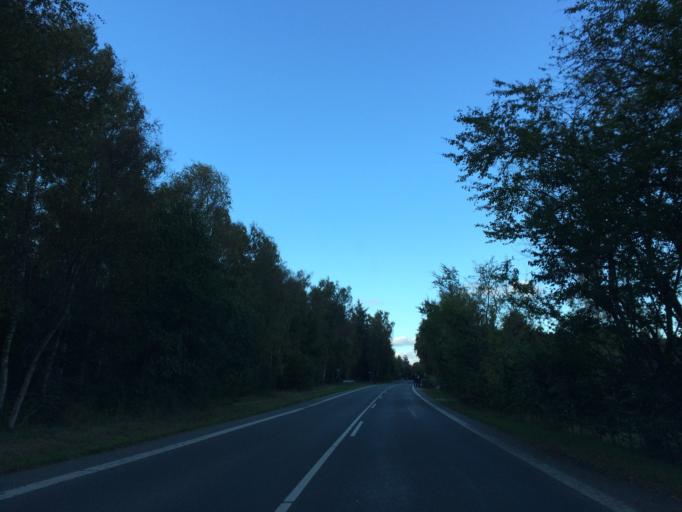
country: DK
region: Central Jutland
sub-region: Skanderborg Kommune
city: Ry
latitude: 56.0973
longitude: 9.7415
